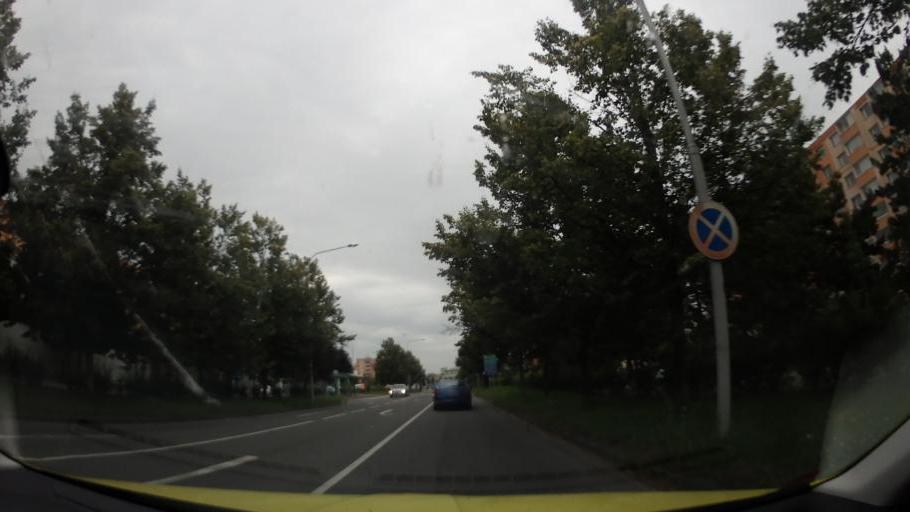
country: CZ
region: Olomoucky
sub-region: Okres Prerov
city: Hranice
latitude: 49.5536
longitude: 17.7356
